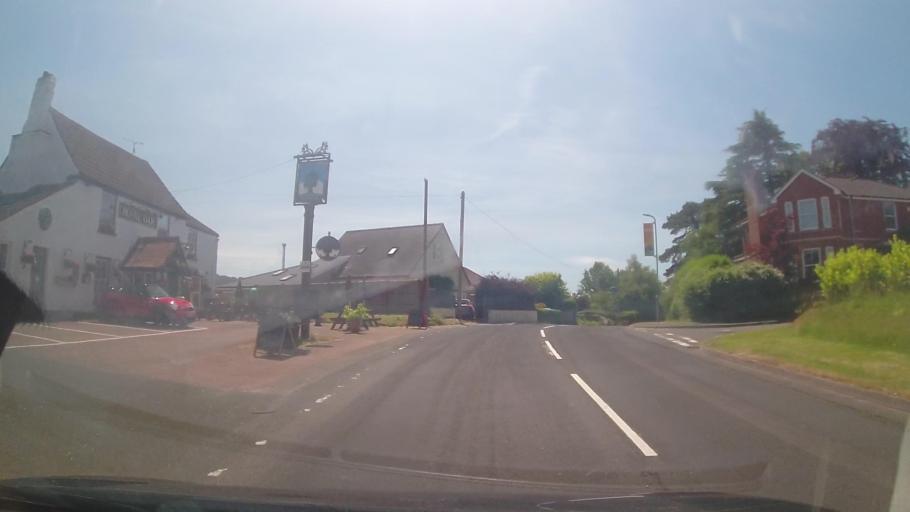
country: GB
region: Wales
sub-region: Monmouthshire
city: Monmouth
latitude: 51.8275
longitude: -2.7125
